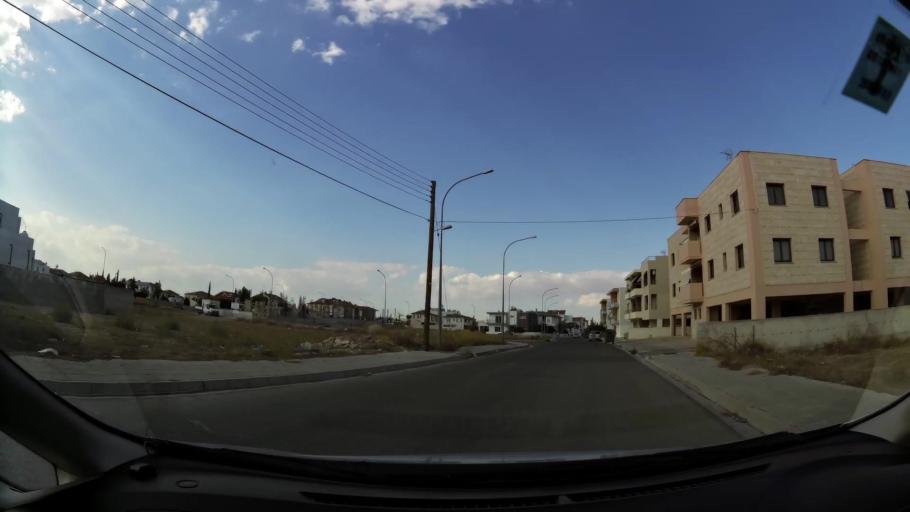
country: CY
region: Larnaka
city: Livadia
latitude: 34.9402
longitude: 33.6120
